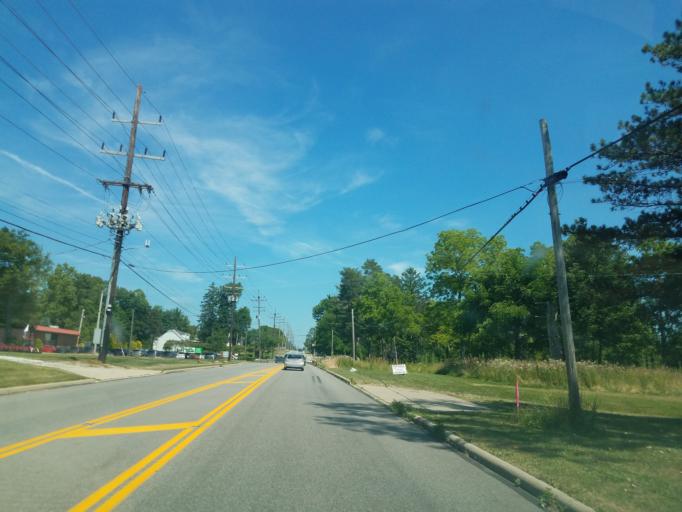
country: US
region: Ohio
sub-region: Geauga County
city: Chesterland
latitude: 41.5224
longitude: -81.3605
